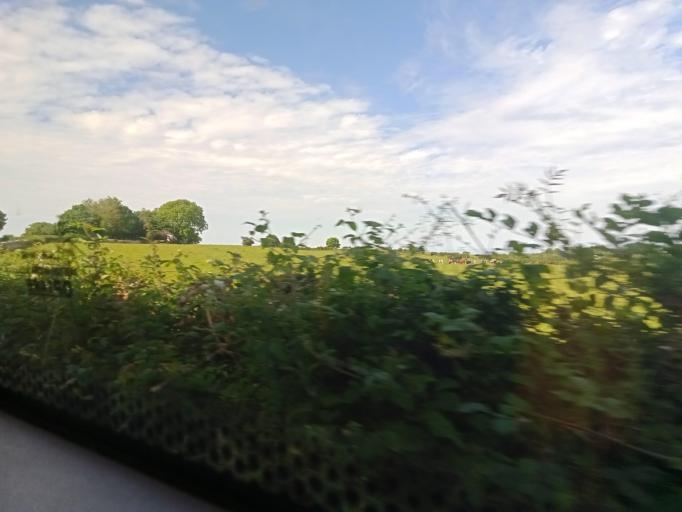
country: GB
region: Wales
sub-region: Anglesey
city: Llangoed
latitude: 53.3013
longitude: -4.0777
